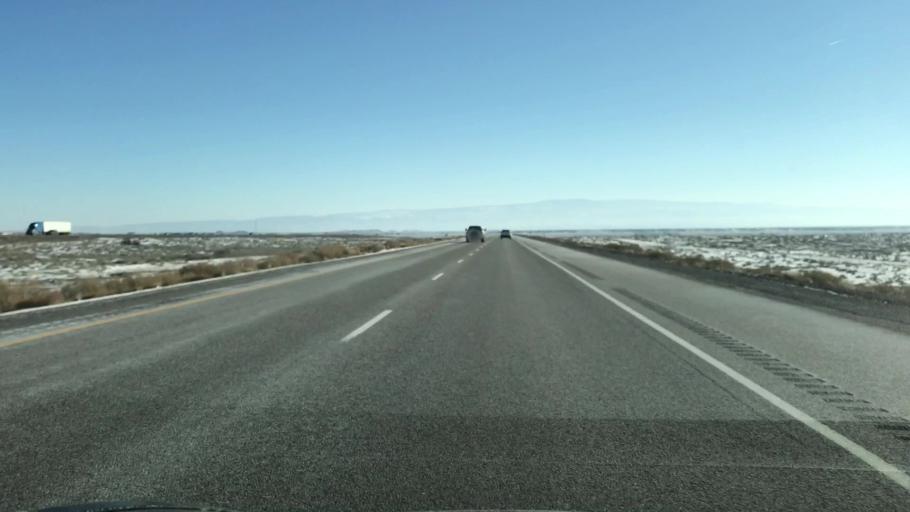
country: US
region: Utah
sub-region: Grand County
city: Moab
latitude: 38.9331
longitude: -109.4455
